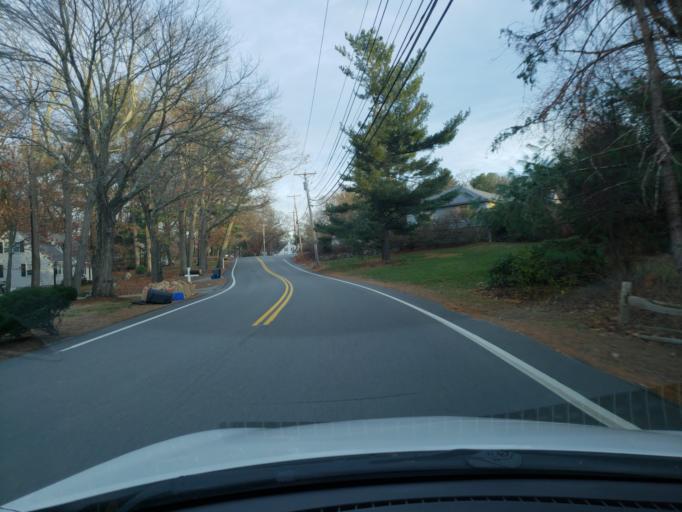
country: US
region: Massachusetts
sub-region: Essex County
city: Lawrence
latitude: 42.6697
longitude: -71.1790
